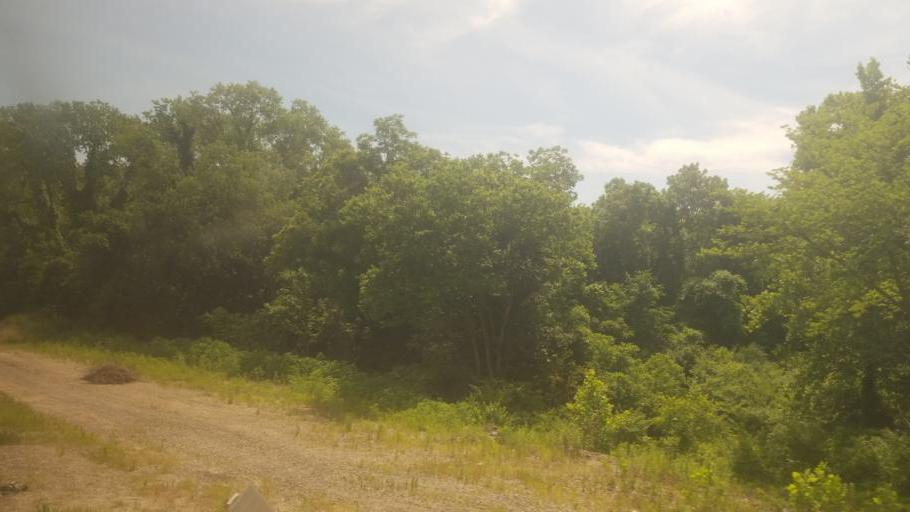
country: US
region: Missouri
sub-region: Jackson County
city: East Independence
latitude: 39.1587
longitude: -94.3663
